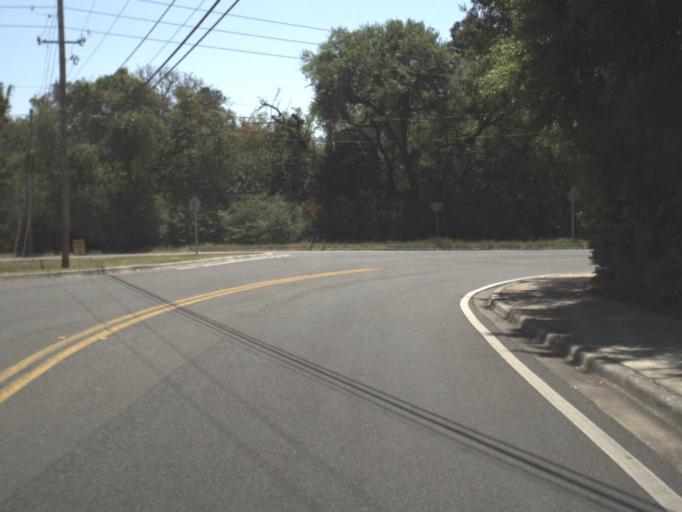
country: US
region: Florida
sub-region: Escambia County
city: Ferry Pass
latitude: 30.4948
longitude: -87.2329
